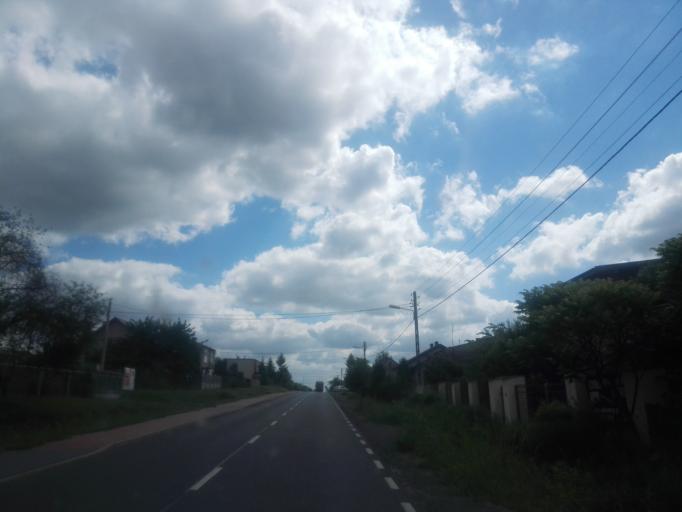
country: PL
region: Silesian Voivodeship
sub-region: Powiat czestochowski
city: Mstow
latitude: 50.7973
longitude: 19.2632
